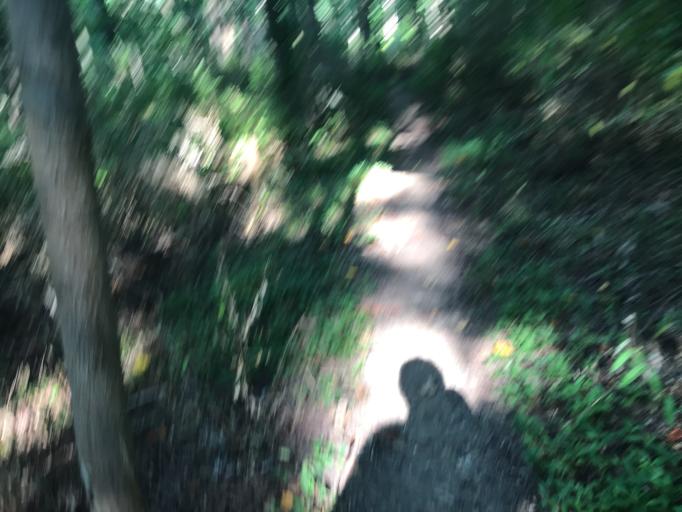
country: US
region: Delaware
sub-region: New Castle County
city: Newark
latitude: 39.7219
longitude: -75.7780
